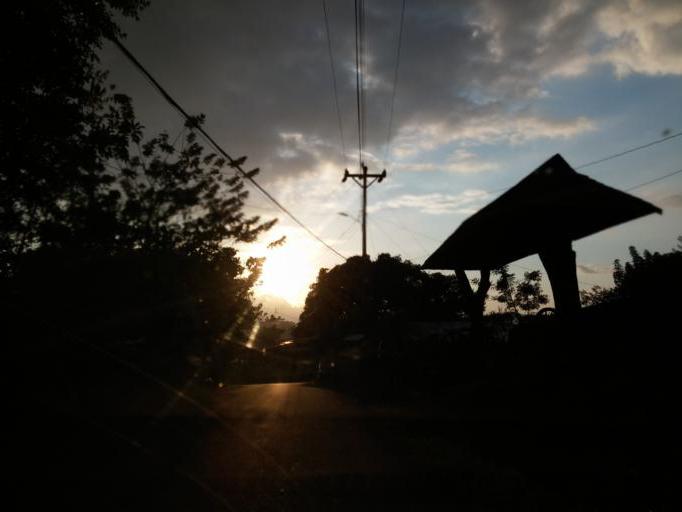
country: CR
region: San Jose
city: Palmichal
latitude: 9.8487
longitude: -84.2314
